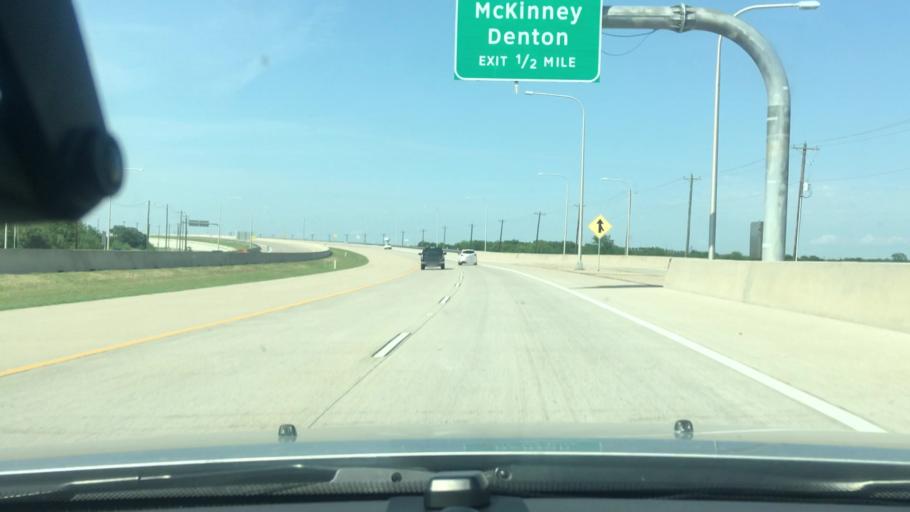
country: US
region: Texas
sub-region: Collin County
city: Prosper
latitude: 33.2032
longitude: -96.8234
